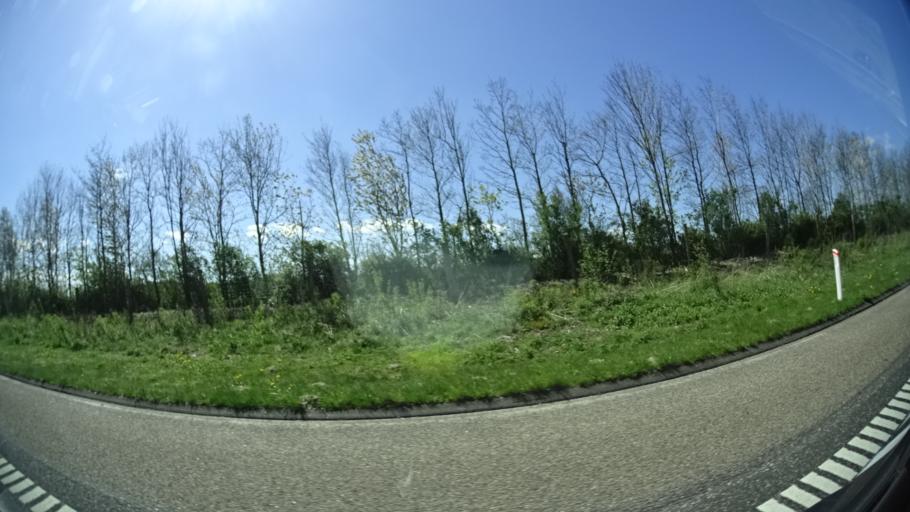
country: DK
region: Central Jutland
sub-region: Arhus Kommune
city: Trige
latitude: 56.3025
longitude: 10.1238
